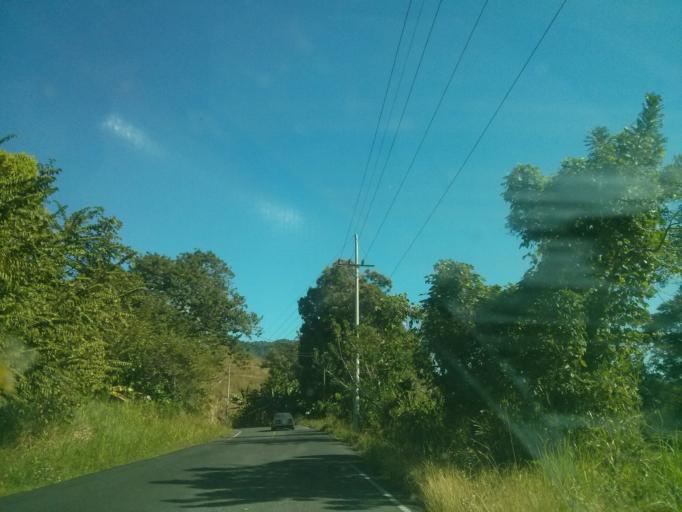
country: CR
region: Puntarenas
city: Paquera
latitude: 9.7609
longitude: -84.9844
